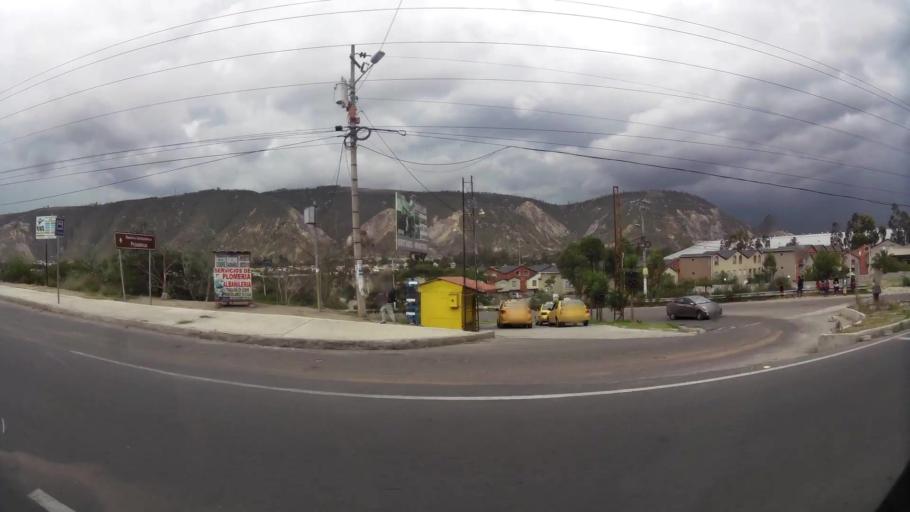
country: EC
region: Pichincha
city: Quito
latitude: -0.0308
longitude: -78.4528
